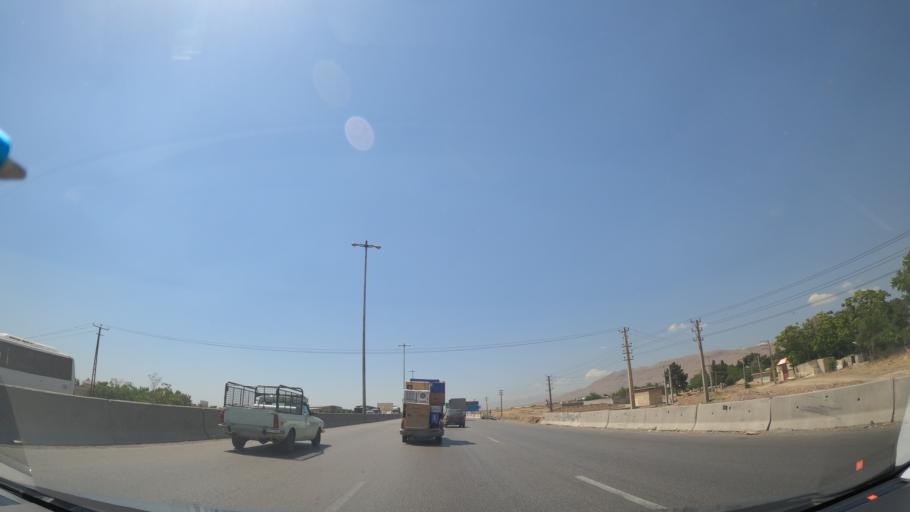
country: IR
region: Alborz
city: Karaj
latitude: 35.8728
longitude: 50.8953
